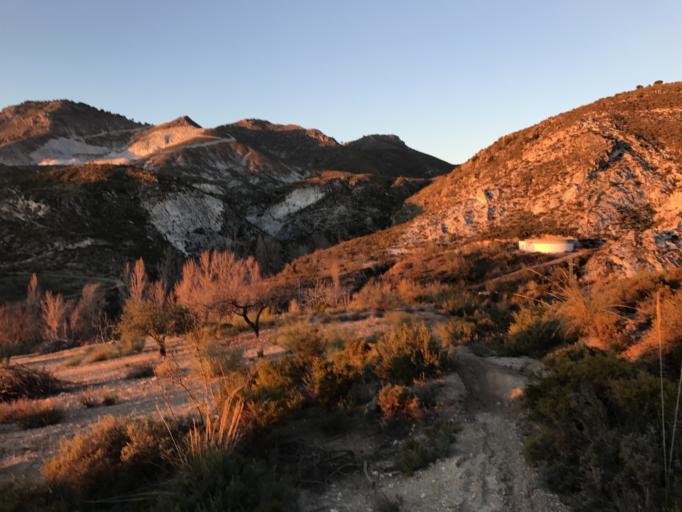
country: ES
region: Andalusia
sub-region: Provincia de Granada
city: Beas de Granada
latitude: 37.2275
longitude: -3.4731
